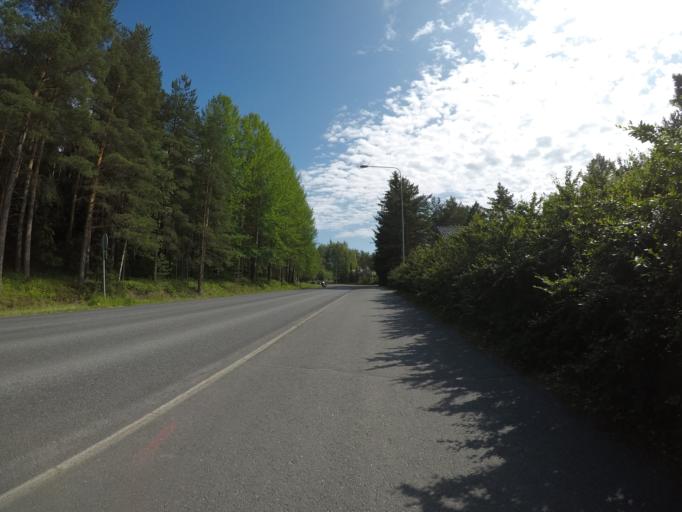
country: FI
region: Haeme
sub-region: Haemeenlinna
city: Haemeenlinna
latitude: 60.9868
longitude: 24.4085
